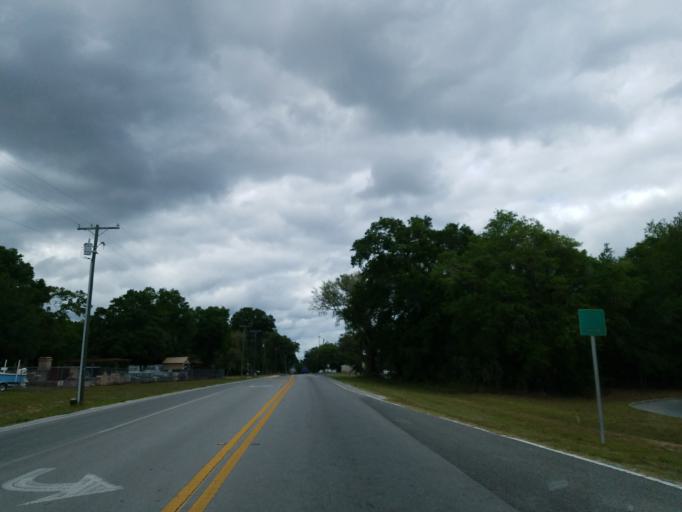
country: US
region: Florida
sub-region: Marion County
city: Ocala
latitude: 29.2820
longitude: -82.1116
